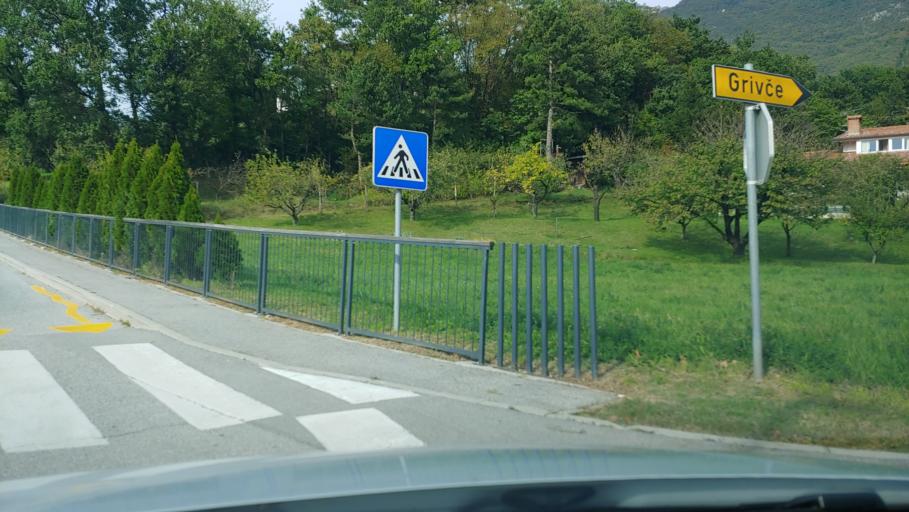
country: SI
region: Ajdovscina
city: Ajdovscina
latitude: 45.8933
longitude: 13.9068
